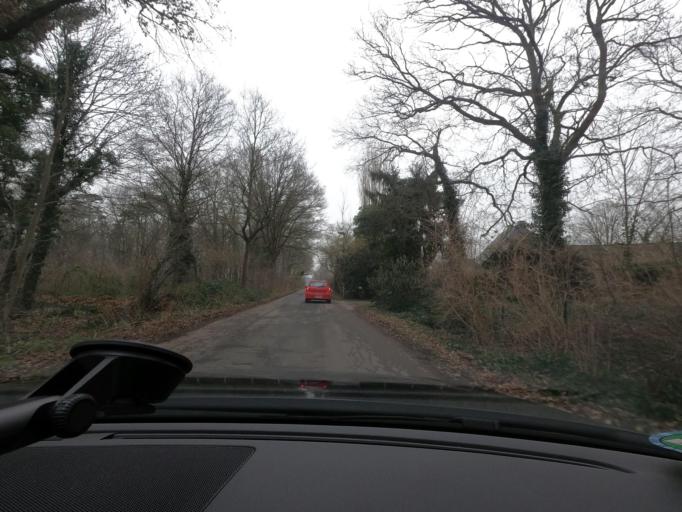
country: DE
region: North Rhine-Westphalia
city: Tonisvorst
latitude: 51.3941
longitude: 6.5222
